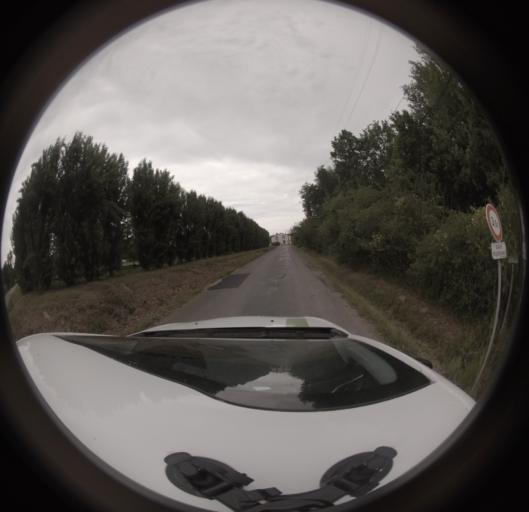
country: FR
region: Midi-Pyrenees
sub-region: Departement du Tarn-et-Garonne
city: Montauban
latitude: 44.0089
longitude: 1.3868
